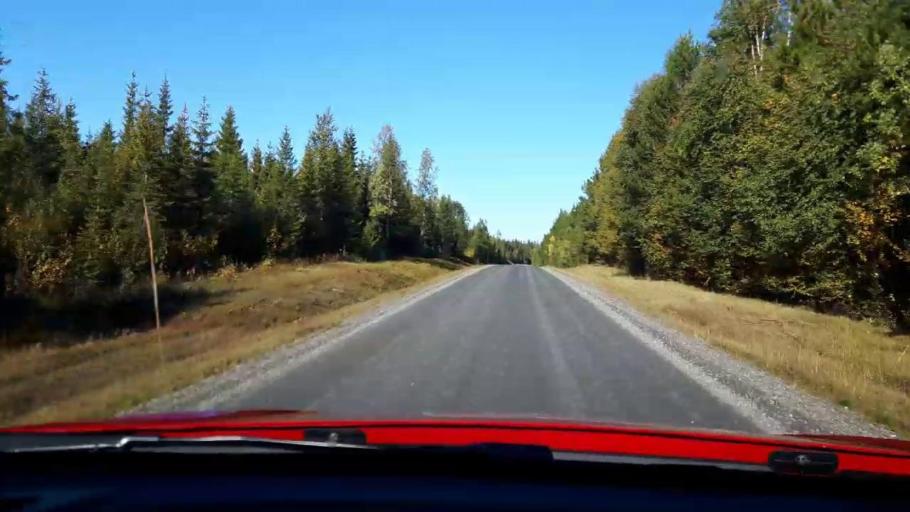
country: NO
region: Nord-Trondelag
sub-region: Lierne
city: Sandvika
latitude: 64.5281
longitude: 14.0516
